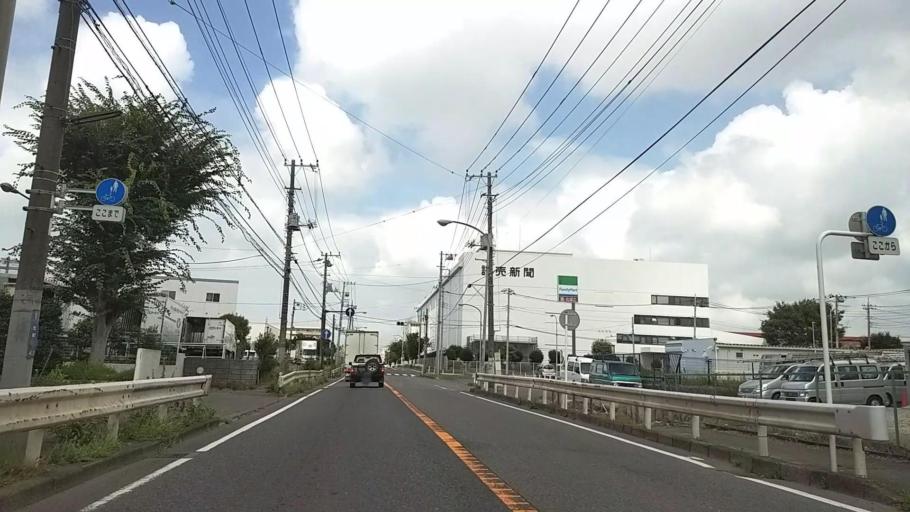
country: JP
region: Kanagawa
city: Minami-rinkan
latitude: 35.4980
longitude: 139.4853
